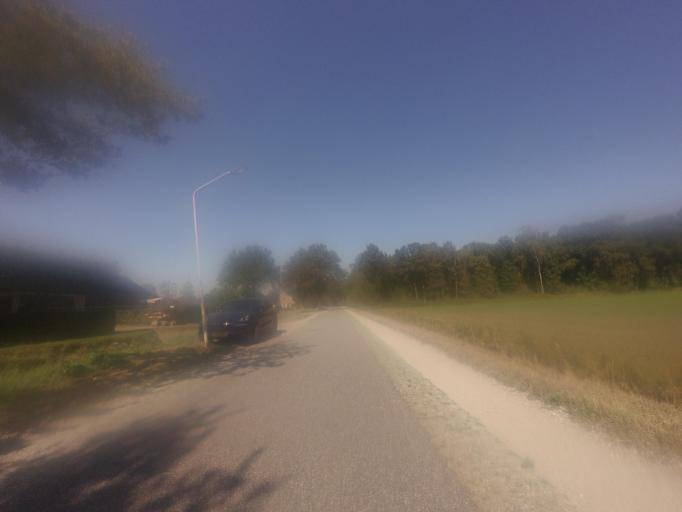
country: NL
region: North Brabant
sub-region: Gemeente Oirschot
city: Oostelbeers
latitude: 51.4838
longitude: 5.2679
